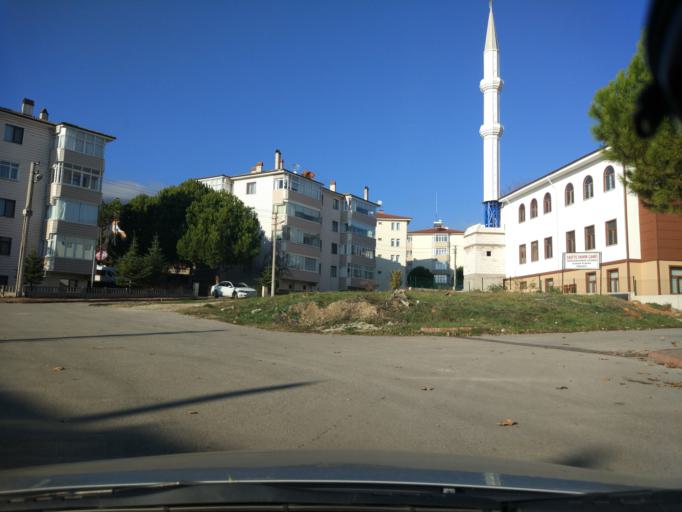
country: TR
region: Karabuk
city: Safranbolu
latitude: 41.2529
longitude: 32.6712
